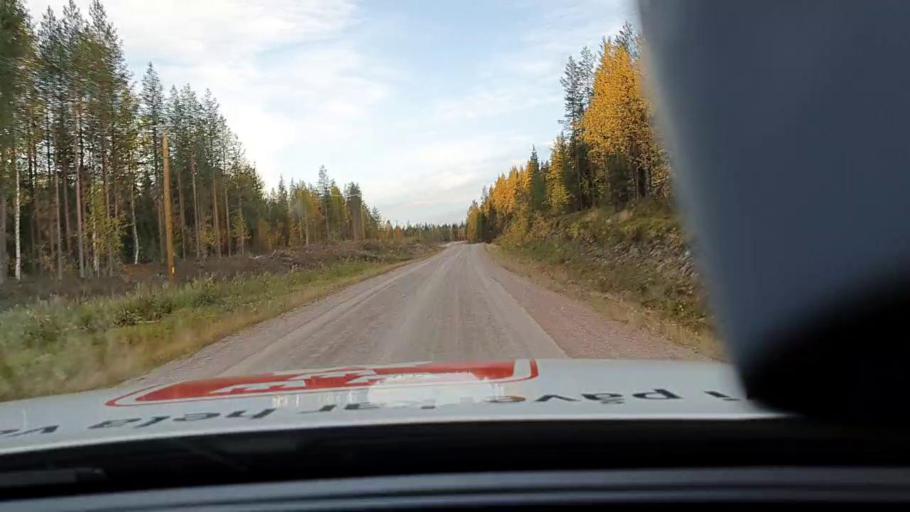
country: SE
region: Norrbotten
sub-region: Overkalix Kommun
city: OEverkalix
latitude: 66.3238
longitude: 22.6289
